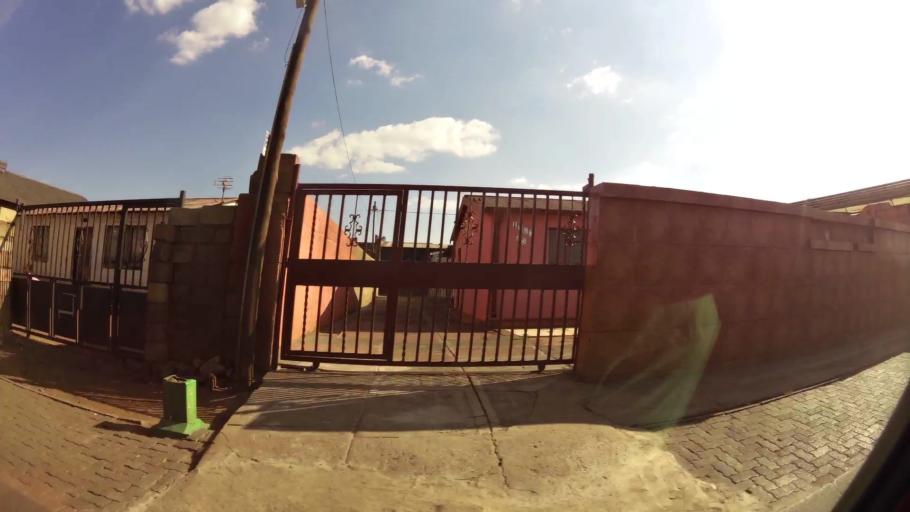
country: ZA
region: Gauteng
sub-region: City of Johannesburg Metropolitan Municipality
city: Soweto
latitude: -26.2214
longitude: 27.8720
